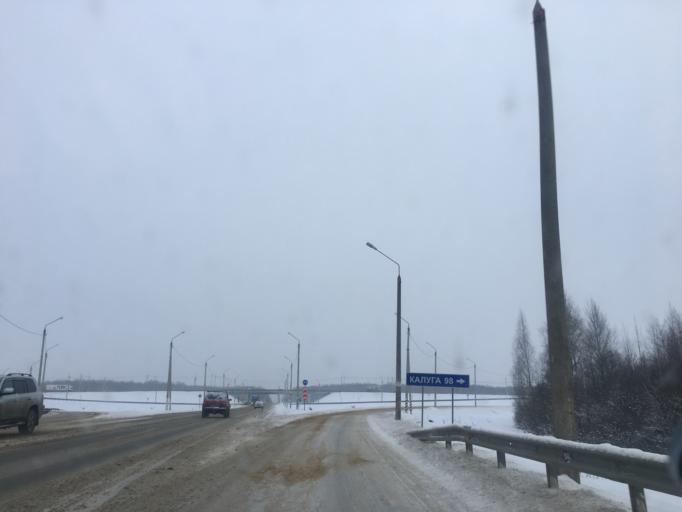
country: RU
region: Tula
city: Kosaya Gora
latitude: 54.1600
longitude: 37.4962
